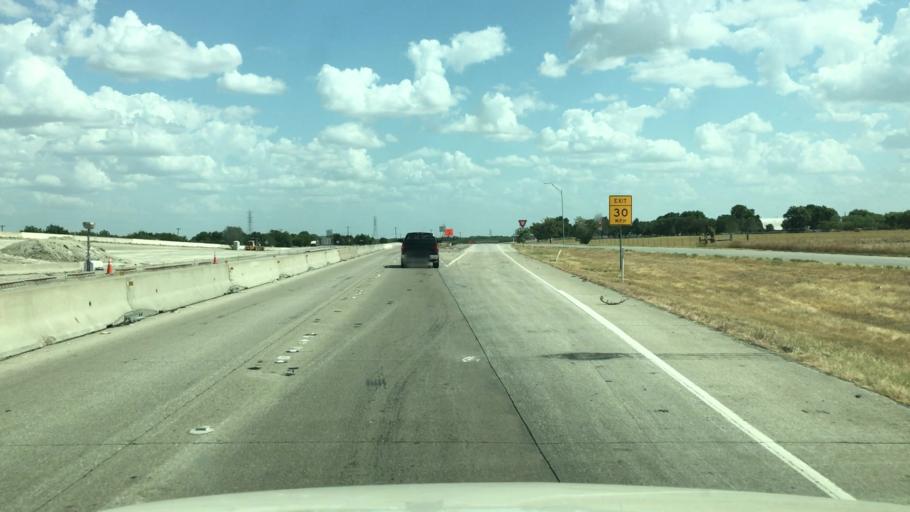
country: US
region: Texas
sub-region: Ellis County
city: Waxahachie
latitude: 32.3631
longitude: -96.8566
